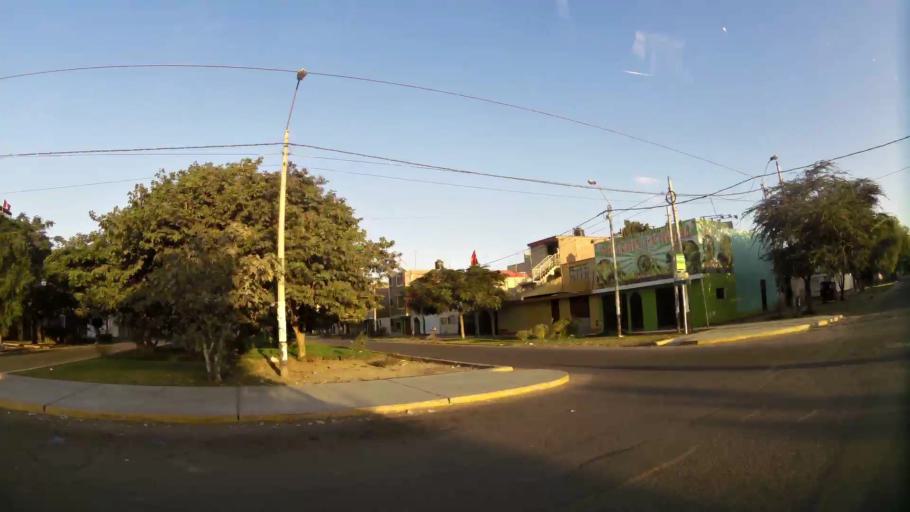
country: PE
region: Ica
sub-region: Provincia de Ica
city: Ica
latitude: -14.0848
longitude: -75.7251
